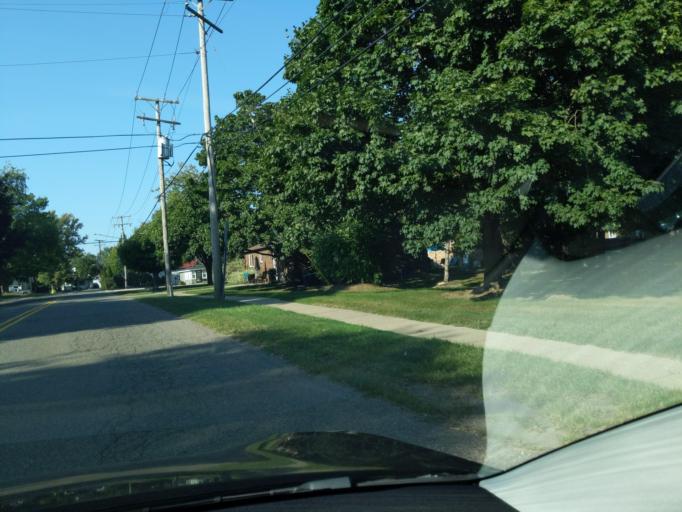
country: US
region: Michigan
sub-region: Oakland County
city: South Lyon
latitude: 42.4588
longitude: -83.6562
